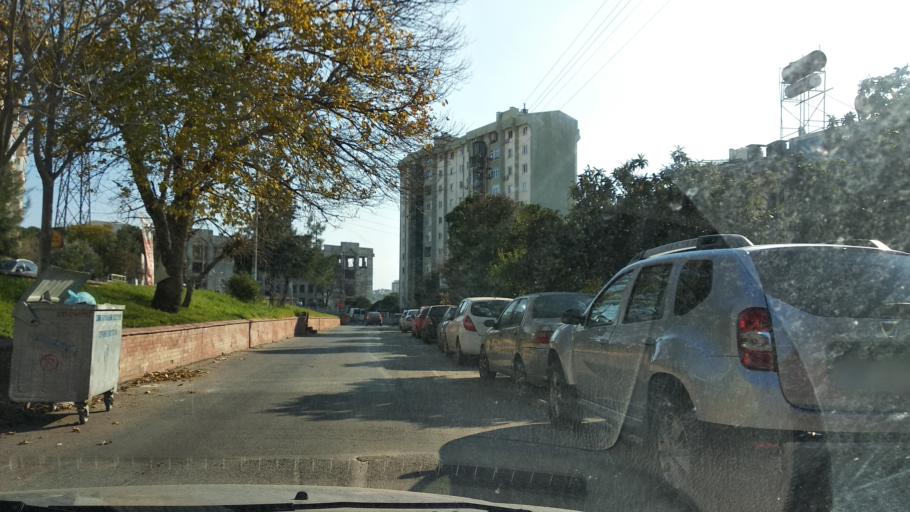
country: TR
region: Izmir
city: Karsiyaka
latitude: 38.4930
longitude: 27.0875
